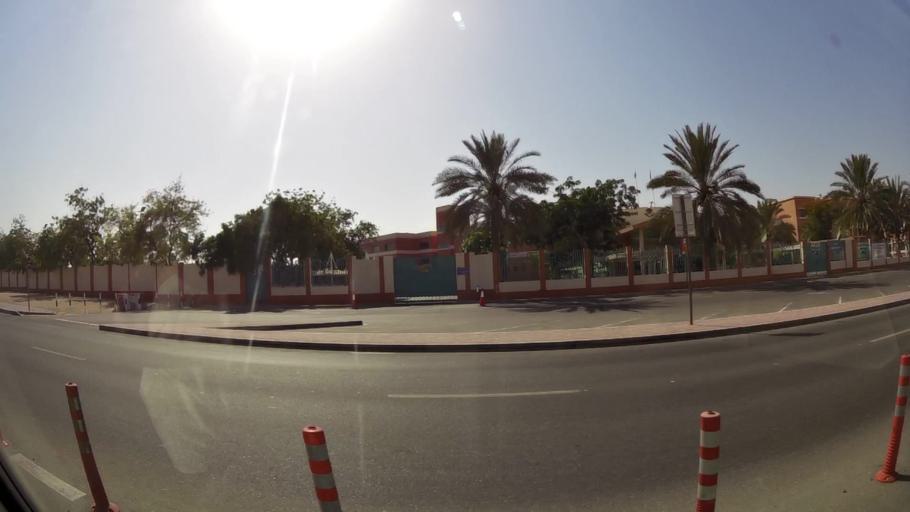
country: AE
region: Ash Shariqah
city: Sharjah
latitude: 25.2781
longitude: 55.3691
